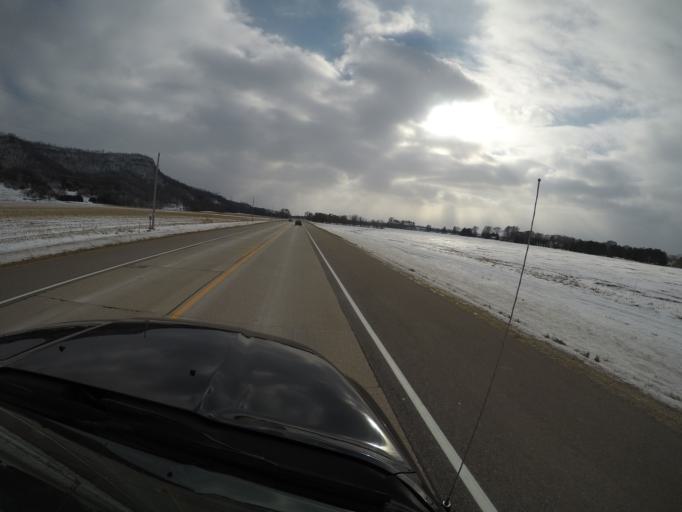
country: US
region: Wisconsin
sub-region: La Crosse County
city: Holmen
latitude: 44.0181
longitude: -91.2885
